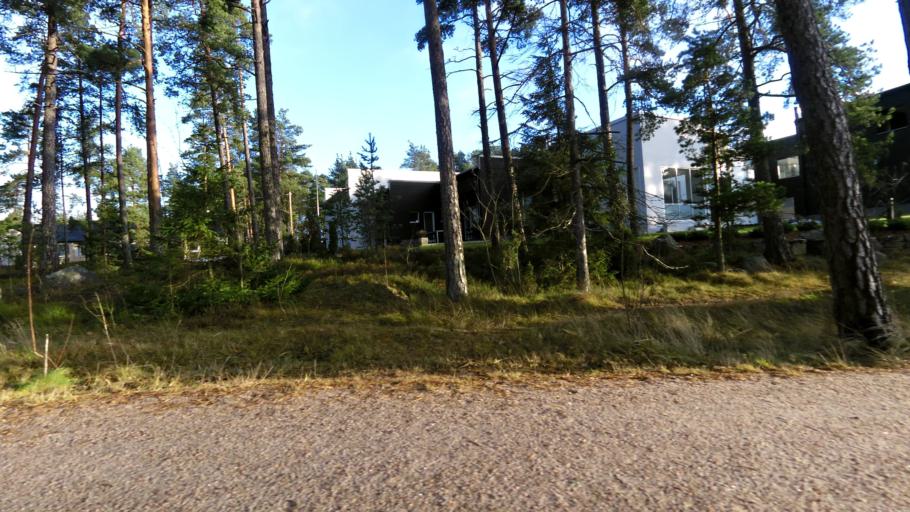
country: FI
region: Uusimaa
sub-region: Helsinki
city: Koukkuniemi
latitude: 60.1512
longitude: 24.7597
